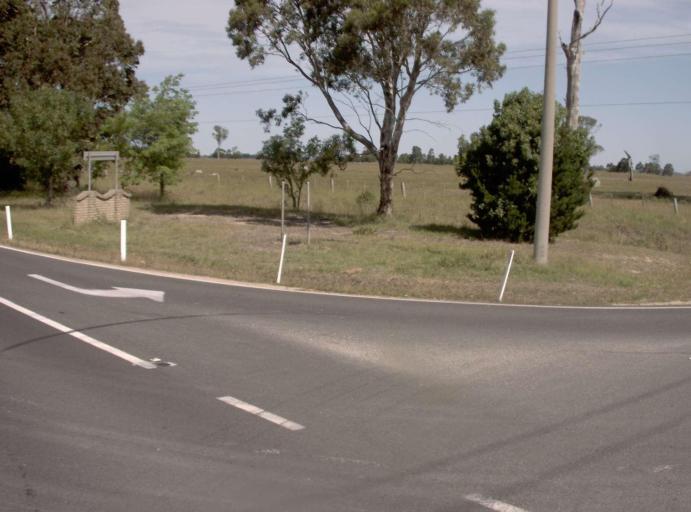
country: AU
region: Victoria
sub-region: East Gippsland
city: Bairnsdale
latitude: -37.8204
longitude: 147.6629
